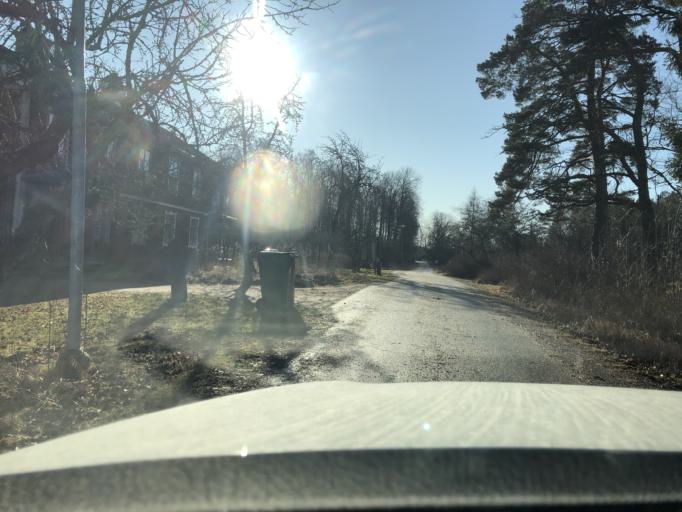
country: SE
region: Uppsala
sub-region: Heby Kommun
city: Tarnsjo
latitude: 60.2940
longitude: 16.8880
